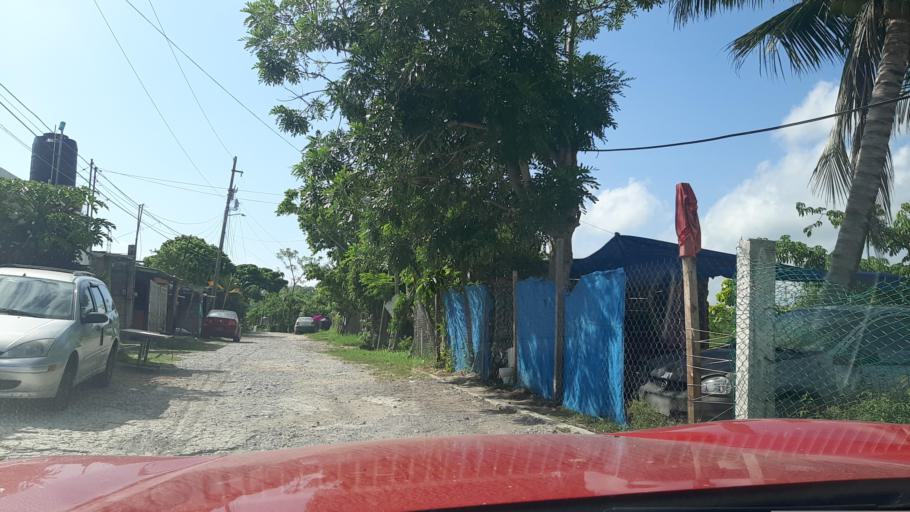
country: MX
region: Veracruz
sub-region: Poza Rica de Hidalgo
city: El Mollejon
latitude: 20.5427
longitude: -97.4103
